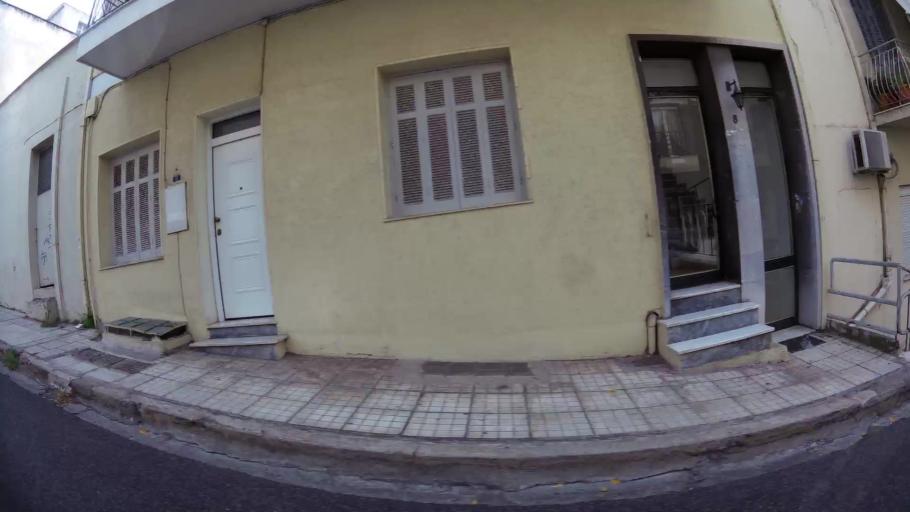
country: GR
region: Attica
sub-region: Nomarchia Athinas
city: Kipseli
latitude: 37.9954
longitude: 23.7536
